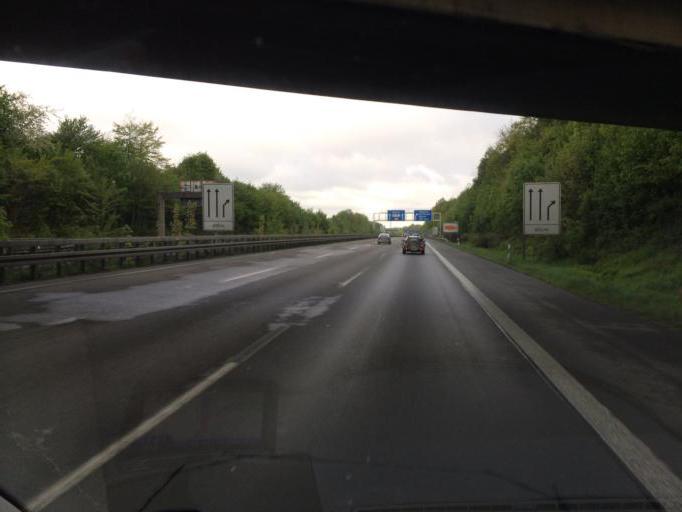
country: DE
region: North Rhine-Westphalia
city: Witten
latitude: 51.4595
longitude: 7.3137
